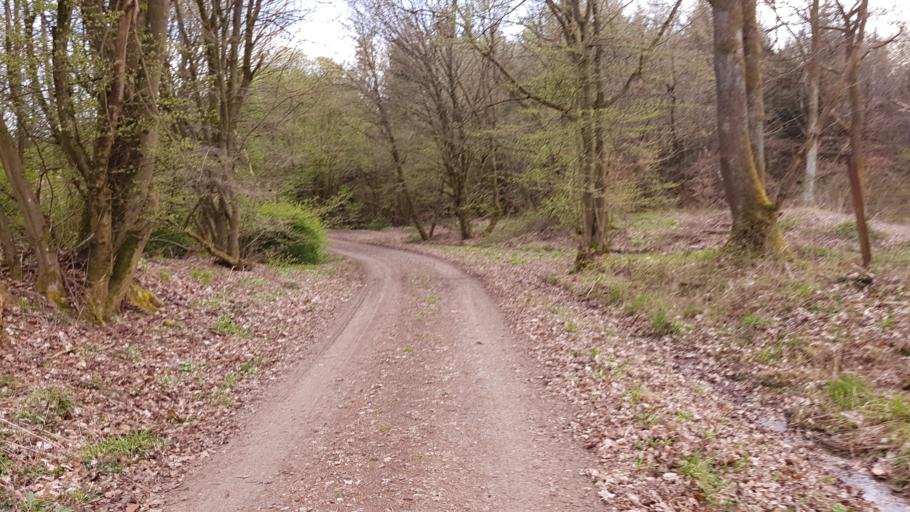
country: DE
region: Hesse
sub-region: Regierungsbezirk Giessen
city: Homberg
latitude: 50.6589
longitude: 9.0350
